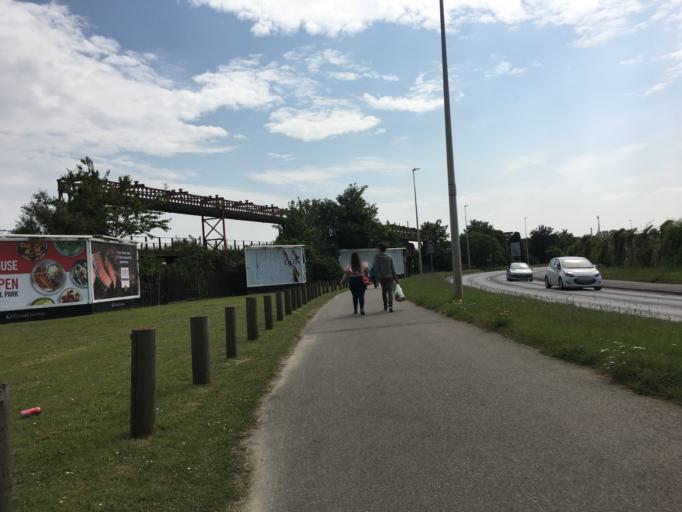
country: GB
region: England
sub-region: Kent
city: Sittingbourne
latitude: 51.3476
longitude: 0.7359
